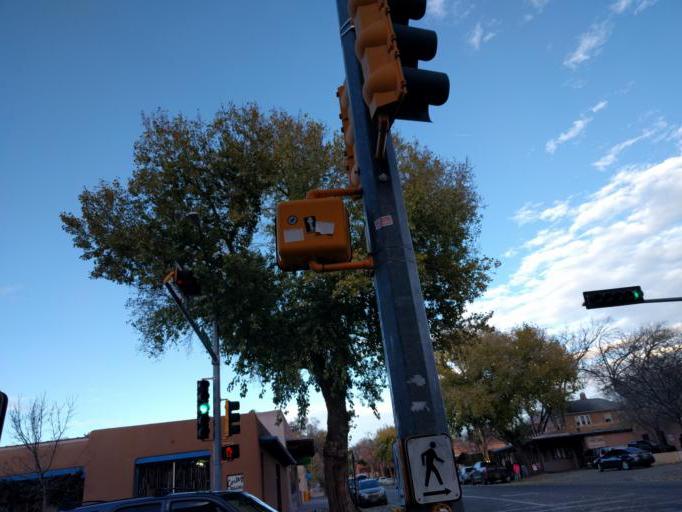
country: US
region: New Mexico
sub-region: Santa Fe County
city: Santa Fe
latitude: 35.6891
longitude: -105.9373
